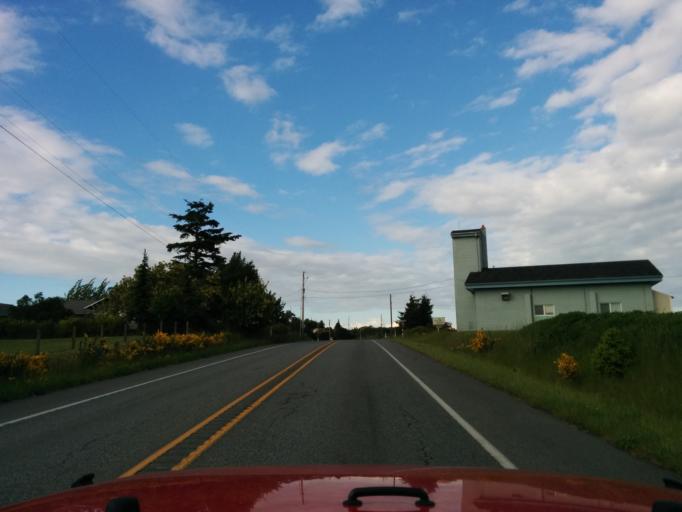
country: US
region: Washington
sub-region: Island County
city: Coupeville
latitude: 48.2370
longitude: -122.7206
